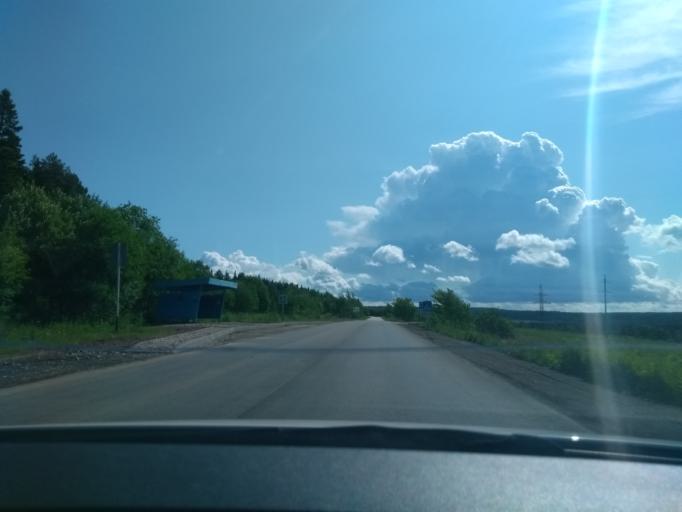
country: RU
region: Perm
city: Kukushtan
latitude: 57.8140
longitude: 56.5516
